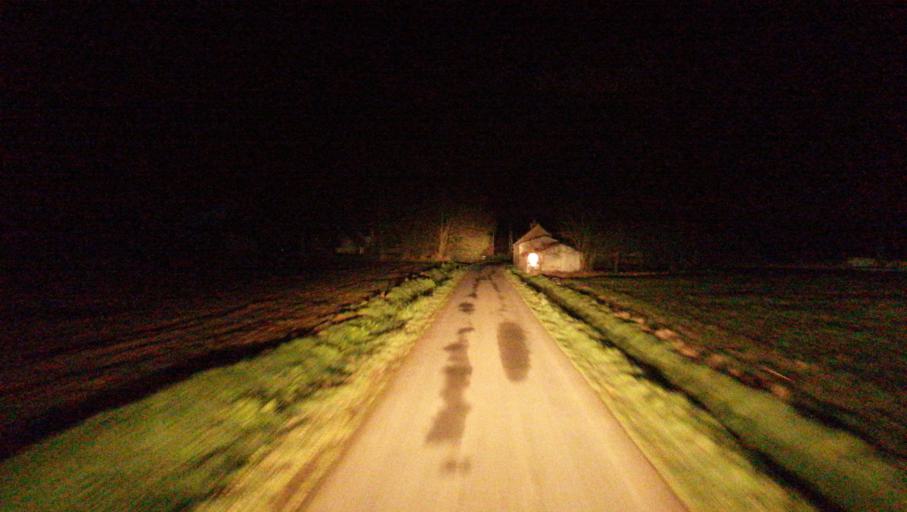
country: FR
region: Brittany
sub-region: Departement des Cotes-d'Armor
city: Saint-Agathon
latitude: 48.5730
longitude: -3.0756
